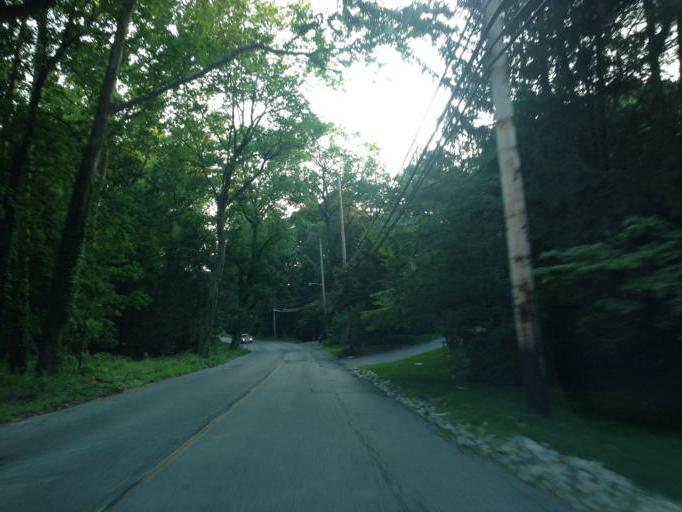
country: US
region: Maryland
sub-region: Baltimore County
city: Mays Chapel
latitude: 39.4017
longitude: -76.6533
